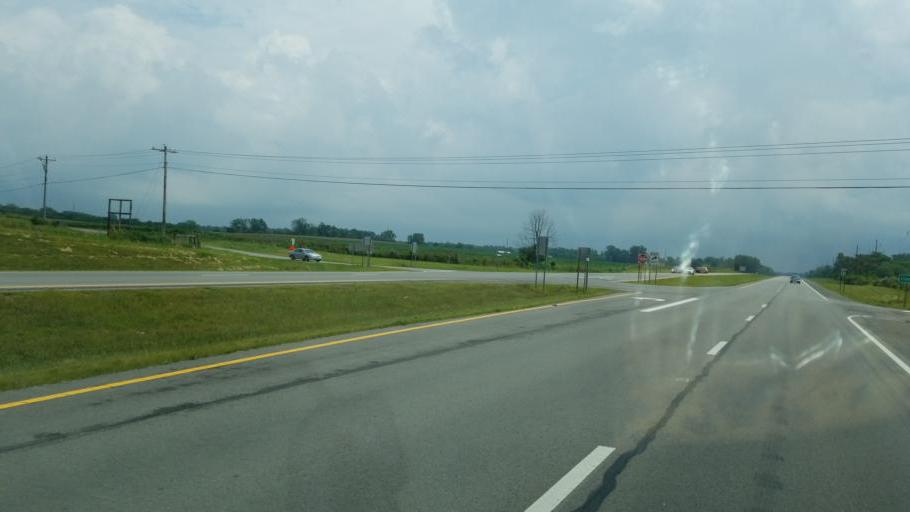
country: US
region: Ohio
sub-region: Logan County
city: Bellefontaine
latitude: 40.4297
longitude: -83.8016
